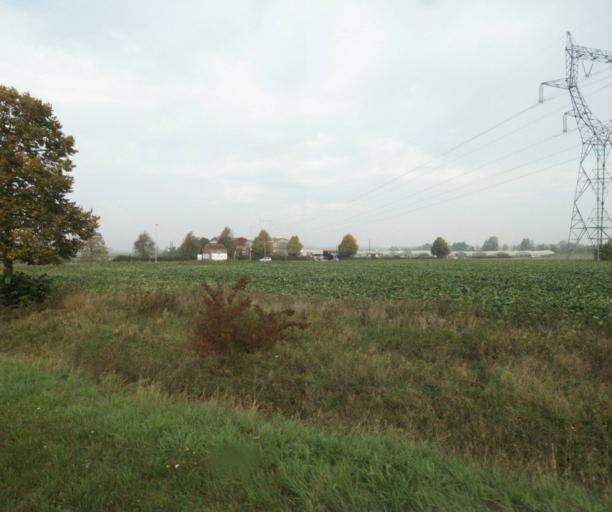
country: FR
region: Nord-Pas-de-Calais
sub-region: Departement du Nord
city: Seclin
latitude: 50.5346
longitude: 3.0170
